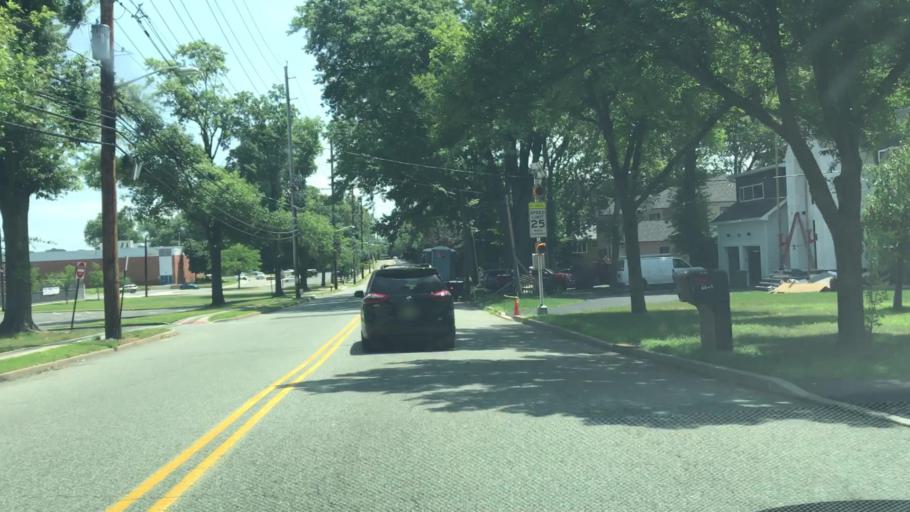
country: US
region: New Jersey
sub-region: Bergen County
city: Paramus
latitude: 40.9276
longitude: -74.0636
